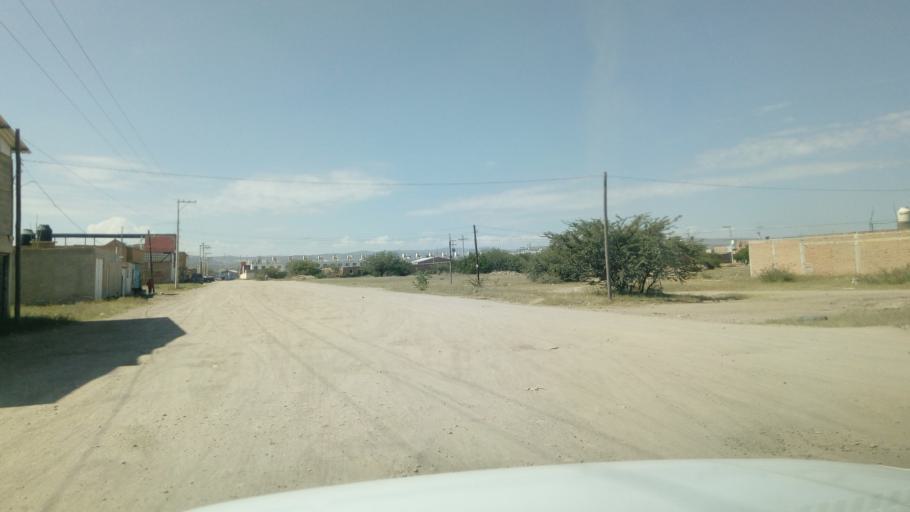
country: MX
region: Durango
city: Victoria de Durango
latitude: 23.9896
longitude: -104.6847
